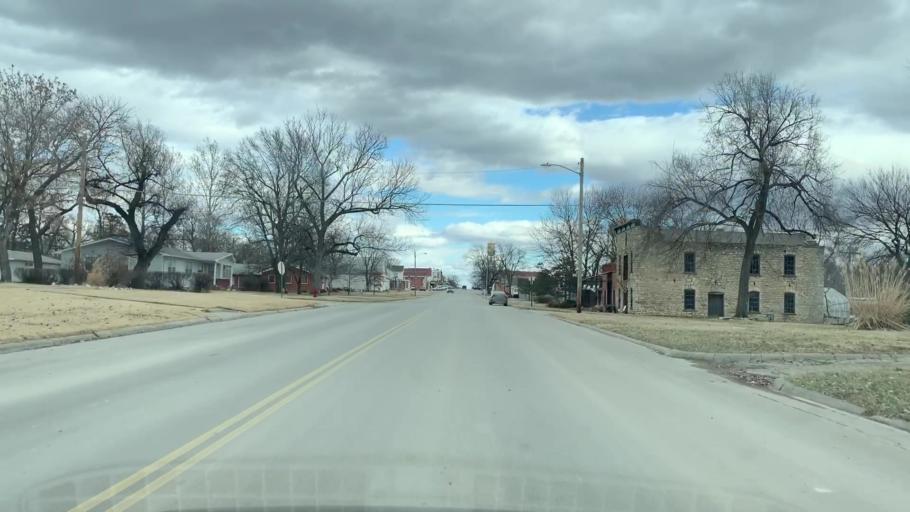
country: US
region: Kansas
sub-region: Allen County
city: Humboldt
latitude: 37.8112
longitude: -95.4426
